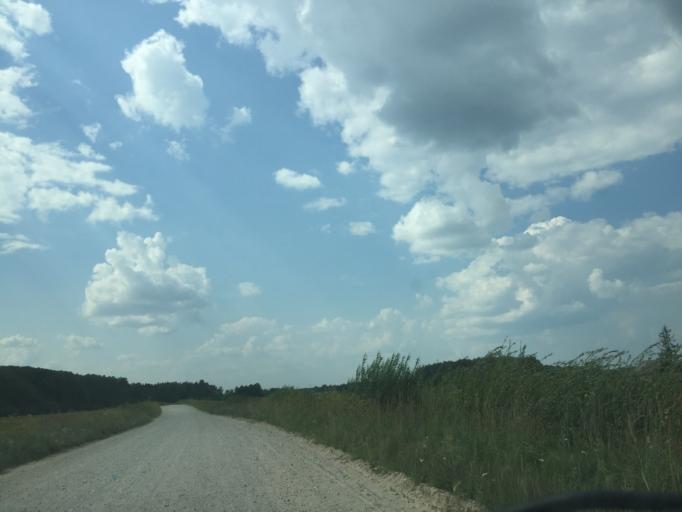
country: LV
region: Auces Novads
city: Auce
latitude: 56.4016
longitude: 23.0575
